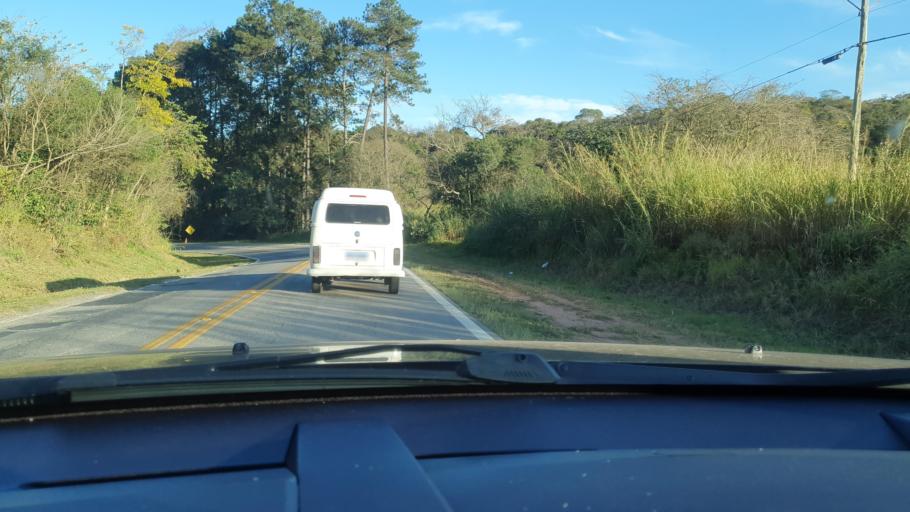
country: BR
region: Sao Paulo
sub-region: Piedade
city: Piedade
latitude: -23.7118
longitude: -47.3973
